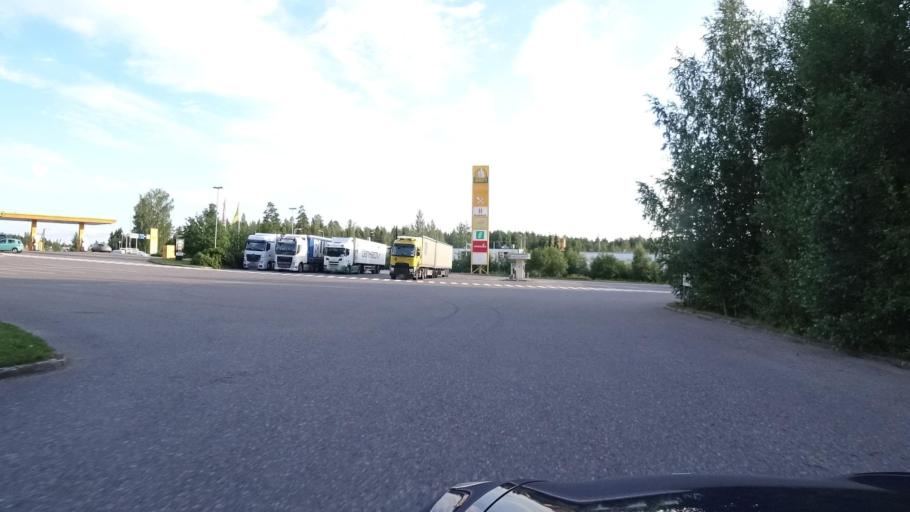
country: FI
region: Uusimaa
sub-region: Helsinki
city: Karkkila
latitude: 60.5197
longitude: 24.2456
